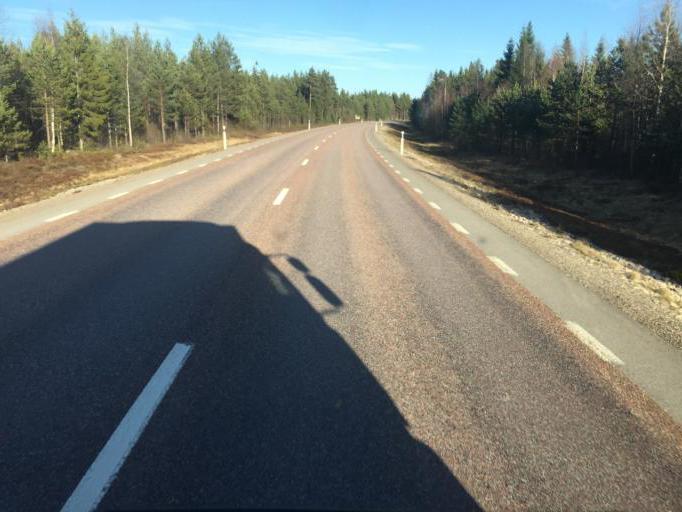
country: SE
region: Dalarna
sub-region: Gagnefs Kommun
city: Mockfjard
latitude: 60.4675
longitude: 14.6875
